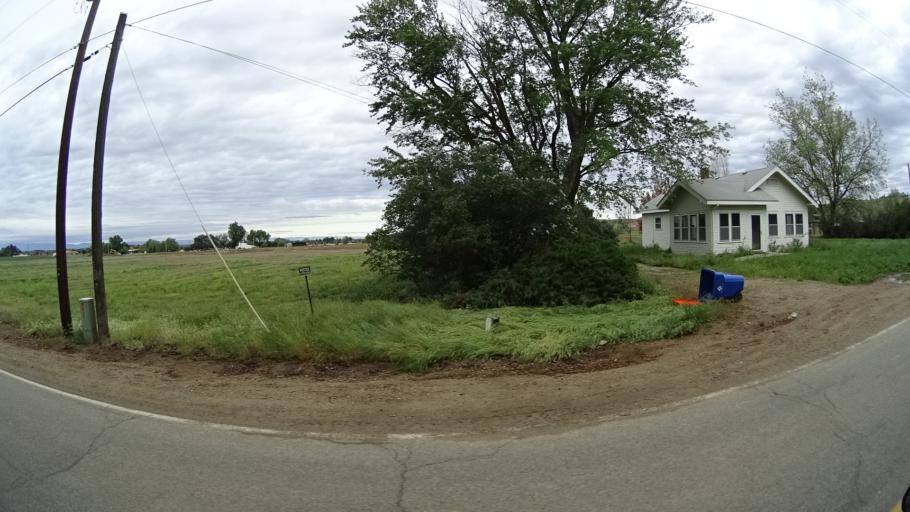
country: US
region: Idaho
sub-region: Ada County
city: Star
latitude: 43.7198
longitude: -116.4830
